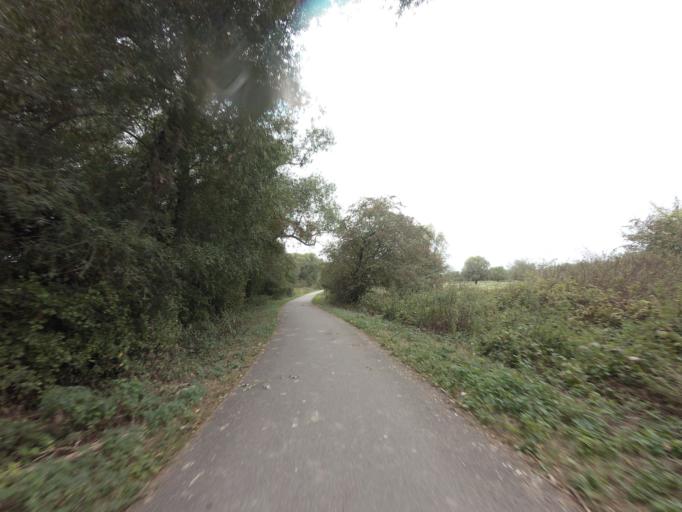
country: NL
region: Gelderland
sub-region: Gemeente Arnhem
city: Burgemeesterswijk
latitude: 51.9716
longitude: 5.8868
